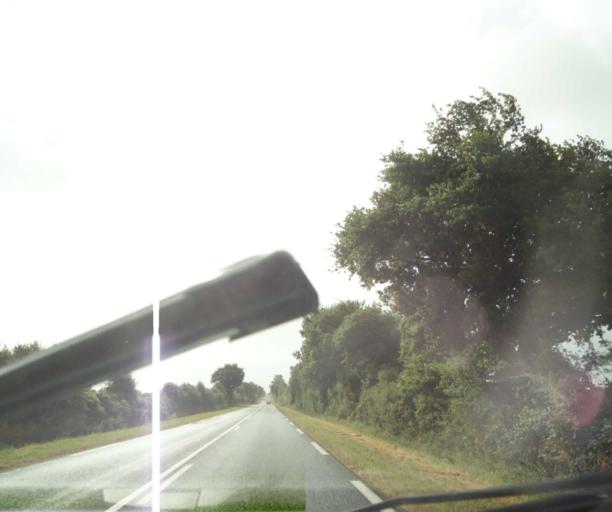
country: FR
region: Pays de la Loire
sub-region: Departement de la Vendee
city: Avrille
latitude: 46.4606
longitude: -1.4487
